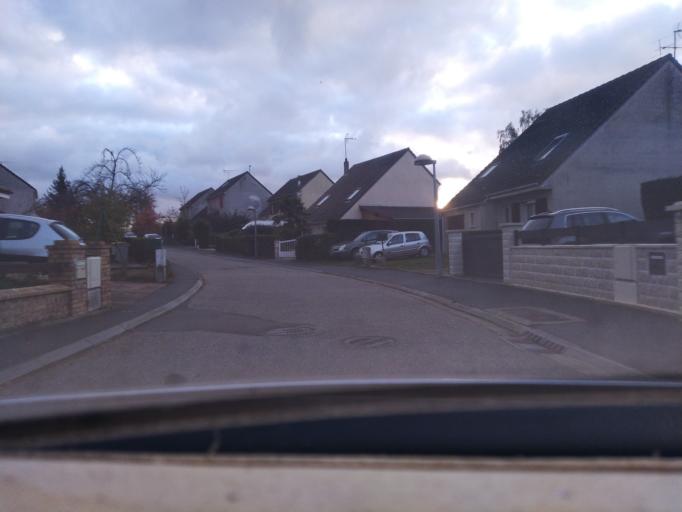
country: FR
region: Haute-Normandie
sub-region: Departement de la Seine-Maritime
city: Yainville
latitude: 49.4572
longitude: 0.8335
